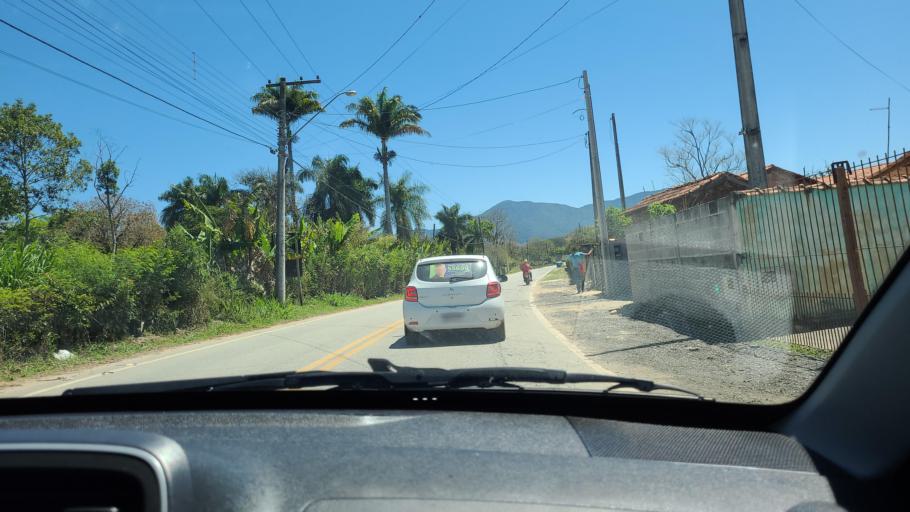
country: BR
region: Sao Paulo
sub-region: Tremembe
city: Tremembe
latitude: -22.8880
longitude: -45.5481
